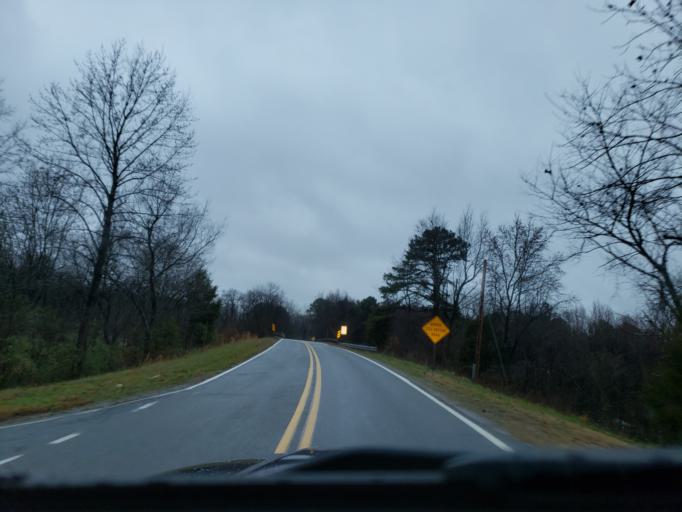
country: US
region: North Carolina
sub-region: Cleveland County
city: White Plains
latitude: 35.1961
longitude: -81.3856
